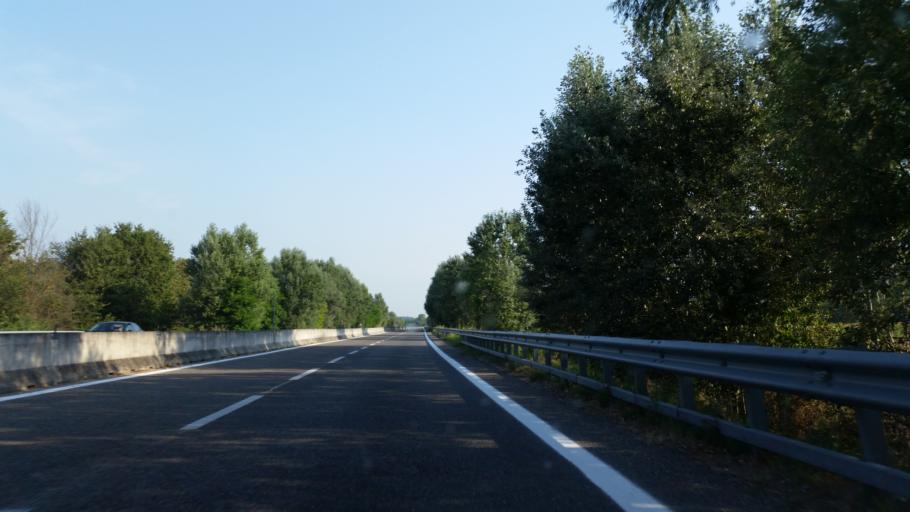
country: IT
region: Piedmont
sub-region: Provincia di Asti
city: Asti
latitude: 44.9315
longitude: 8.2260
